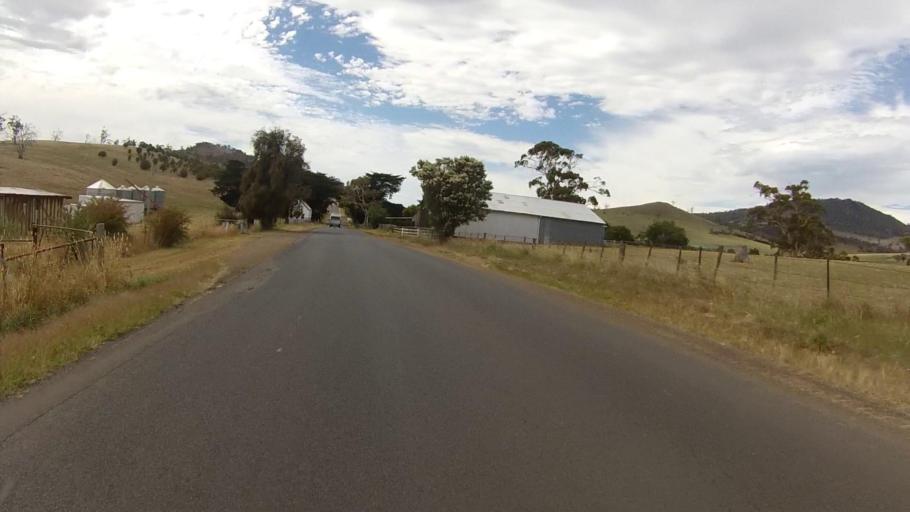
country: AU
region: Tasmania
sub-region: Brighton
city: Old Beach
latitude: -42.7177
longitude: 147.3271
